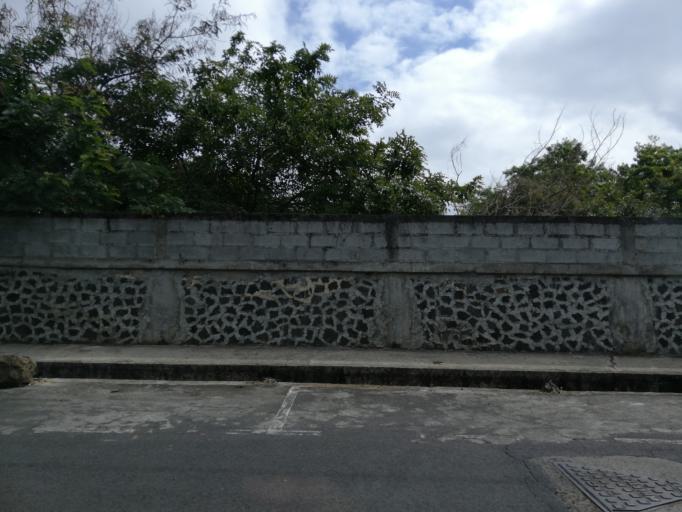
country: MU
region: Port Louis
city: Port Louis
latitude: -20.1627
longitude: 57.4816
